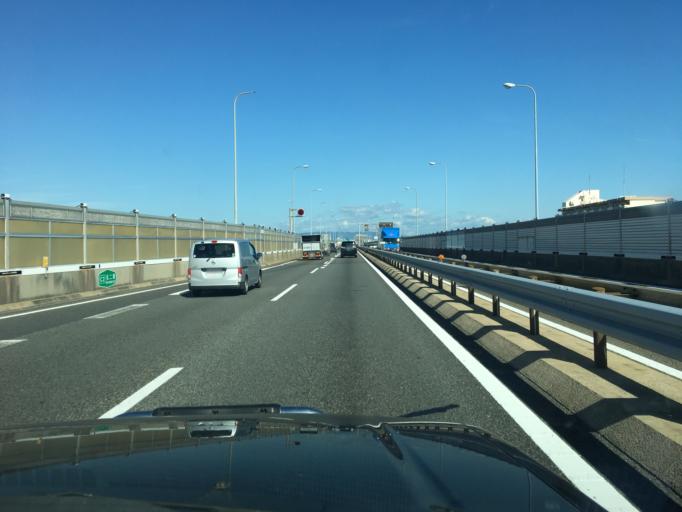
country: JP
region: Aichi
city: Nagoya-shi
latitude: 35.2296
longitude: 136.9208
